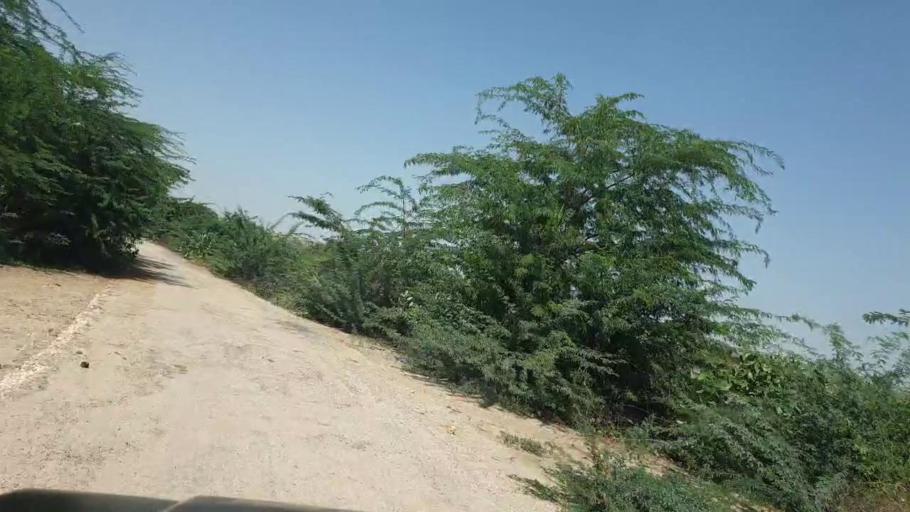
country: PK
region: Sindh
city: Chor
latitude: 25.4098
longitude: 70.3070
